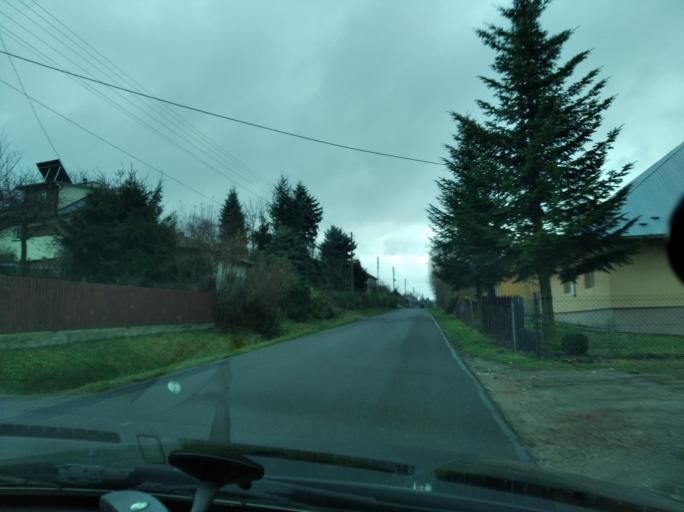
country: PL
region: Subcarpathian Voivodeship
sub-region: Powiat przeworski
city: Sietesz
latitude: 49.9924
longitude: 22.3537
